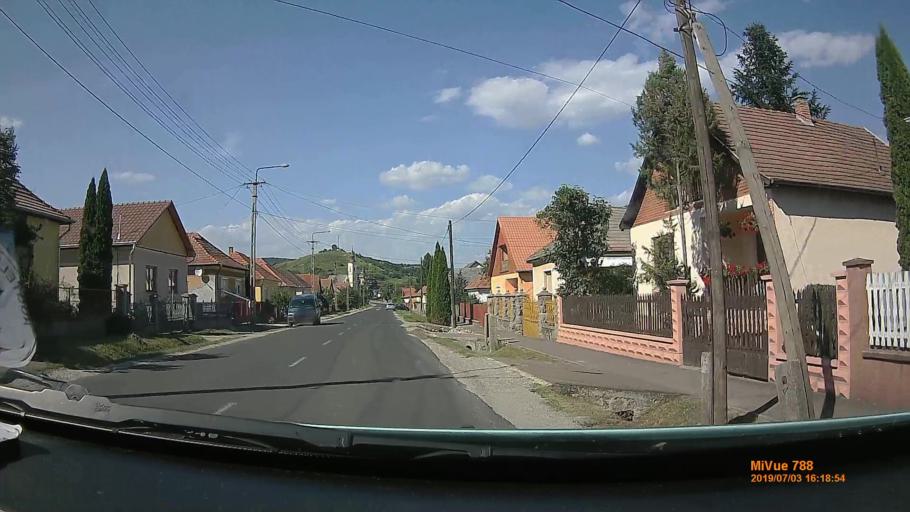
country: HU
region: Borsod-Abauj-Zemplen
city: Sajokaza
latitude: 48.2283
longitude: 20.5024
